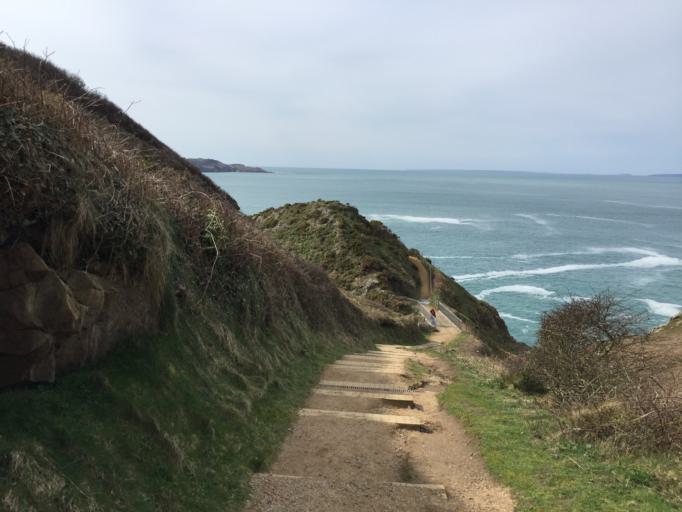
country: JE
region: St Helier
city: Saint Helier
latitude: 49.2516
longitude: -2.1722
